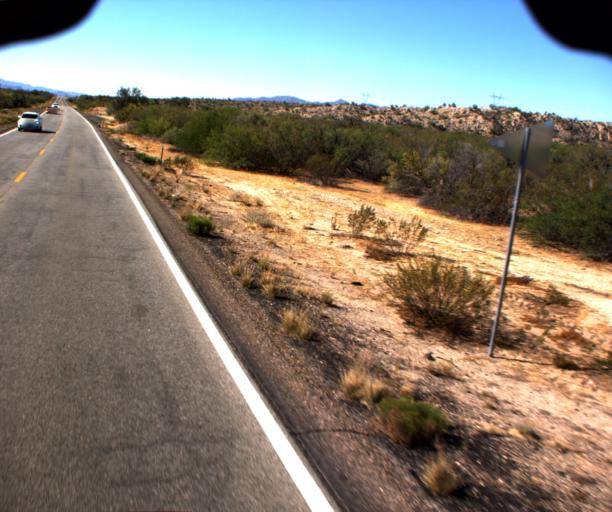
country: US
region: Arizona
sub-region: Yavapai County
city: Bagdad
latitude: 34.7749
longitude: -113.6219
